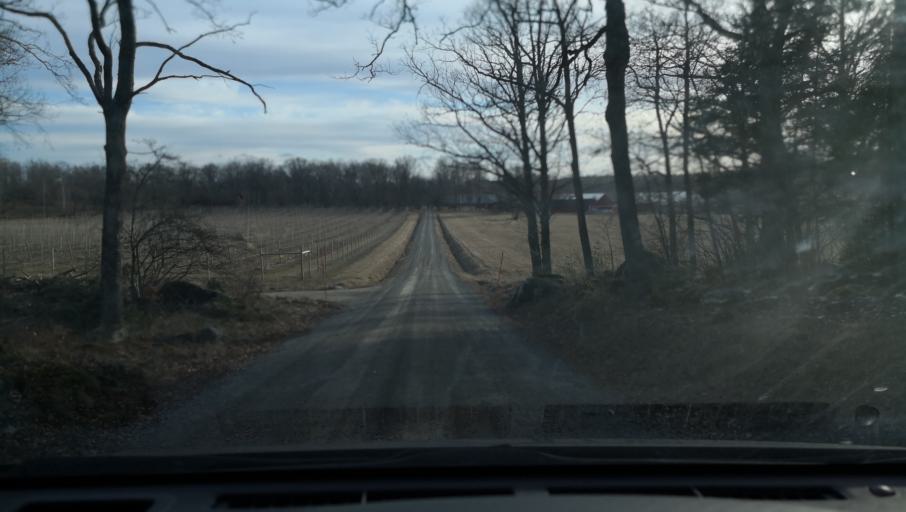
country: SE
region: Uppsala
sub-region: Enkopings Kommun
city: Dalby
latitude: 59.4782
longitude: 17.2542
